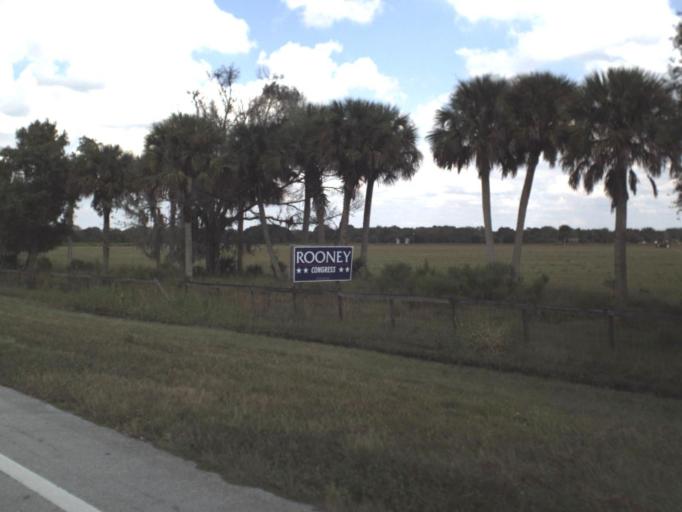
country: US
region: Florida
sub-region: Okeechobee County
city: Okeechobee
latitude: 27.3121
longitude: -80.9061
